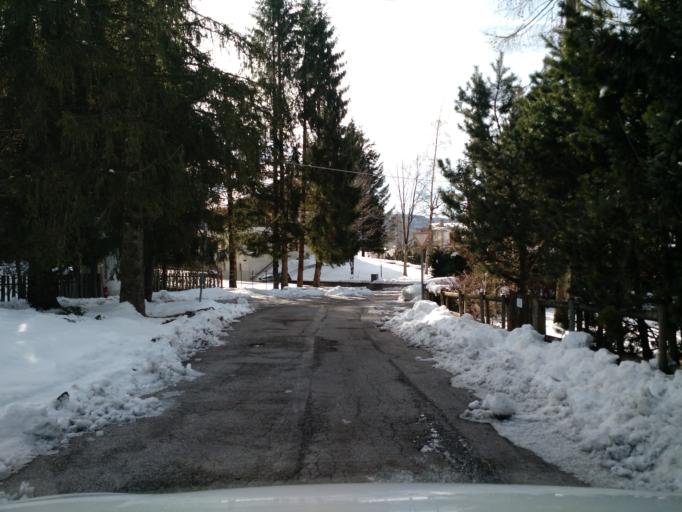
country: IT
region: Veneto
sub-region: Provincia di Vicenza
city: Gallio
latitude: 45.8882
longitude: 11.5368
